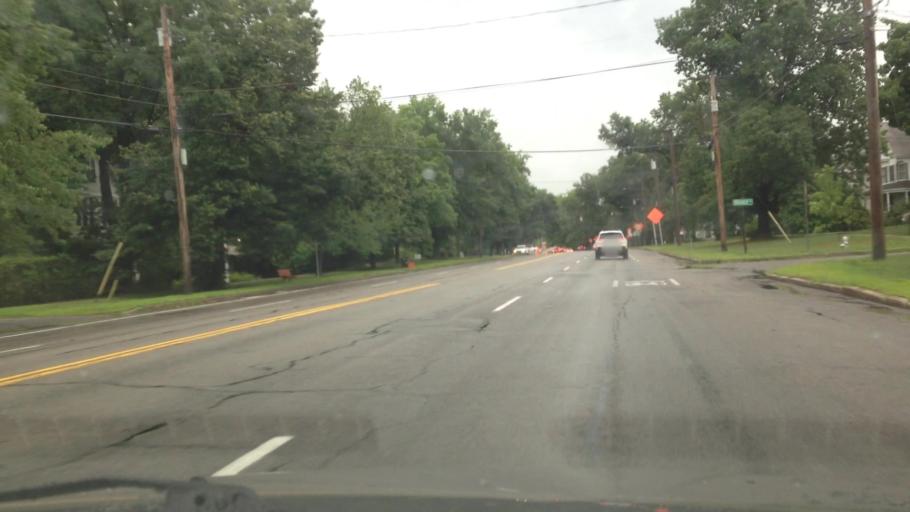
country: US
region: New Hampshire
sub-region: Cheshire County
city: Keene
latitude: 42.9250
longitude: -72.2771
